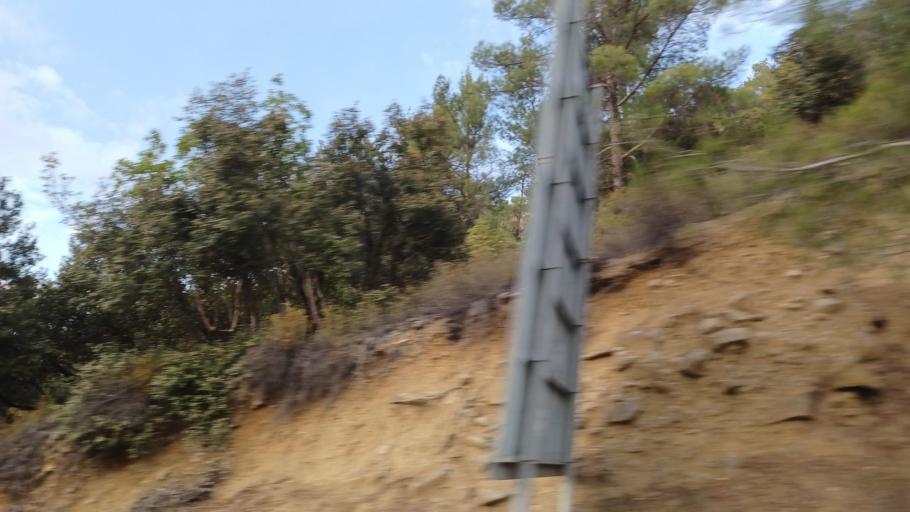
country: CY
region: Lefkosia
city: Kakopetria
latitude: 34.9645
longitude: 32.9255
